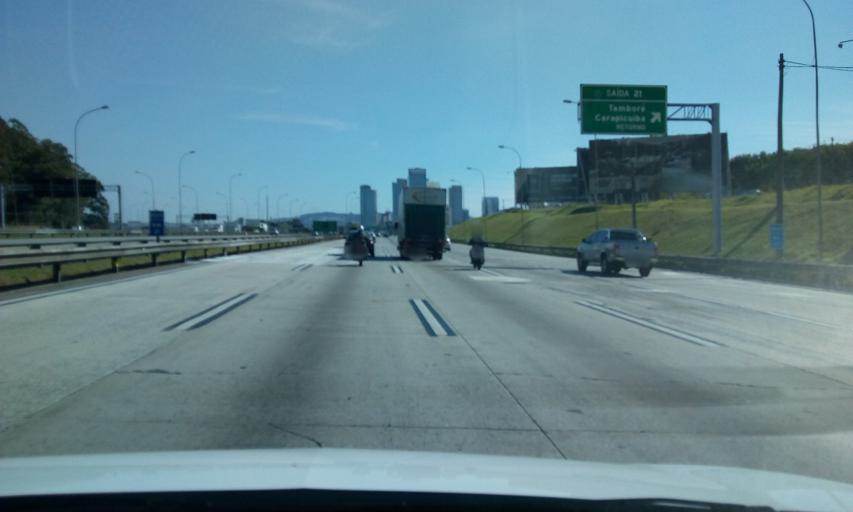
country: BR
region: Sao Paulo
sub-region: Carapicuiba
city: Carapicuiba
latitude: -23.5079
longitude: -46.8261
